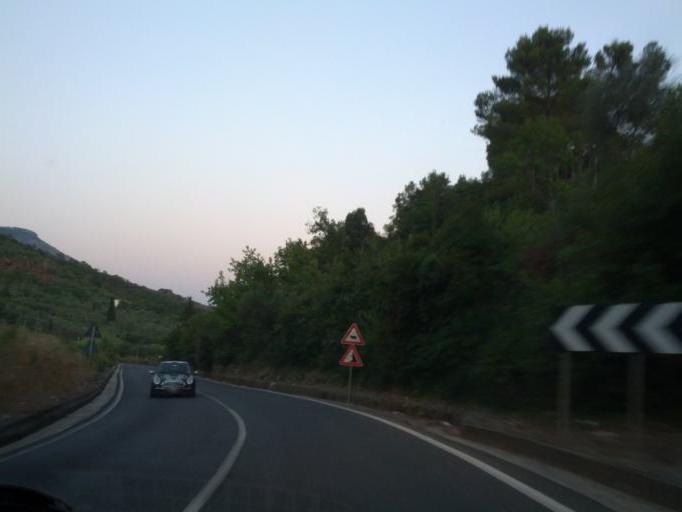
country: IT
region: Latium
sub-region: Provincia di Latina
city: Itri
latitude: 41.3003
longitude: 13.5042
